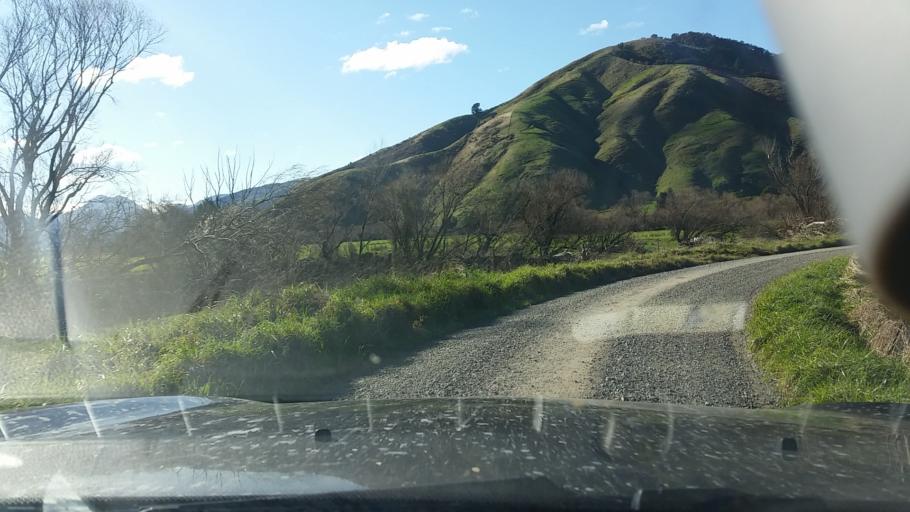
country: NZ
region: Marlborough
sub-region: Marlborough District
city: Picton
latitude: -41.3323
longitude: 173.7659
